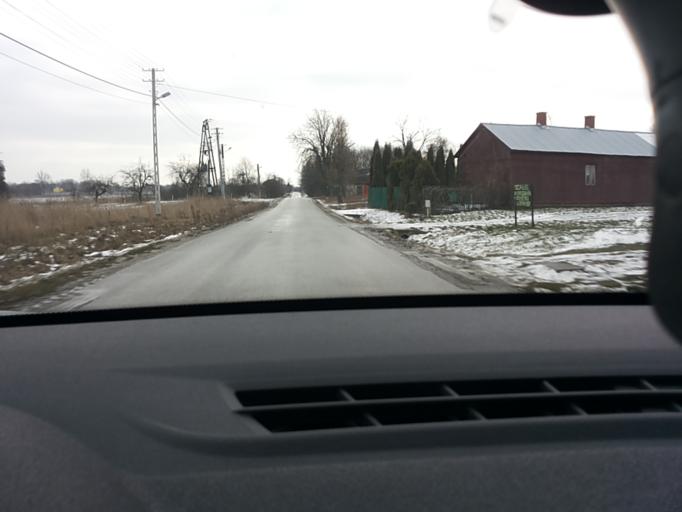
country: PL
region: Lodz Voivodeship
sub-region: Powiat skierniewicki
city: Makow
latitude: 51.9998
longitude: 20.0751
